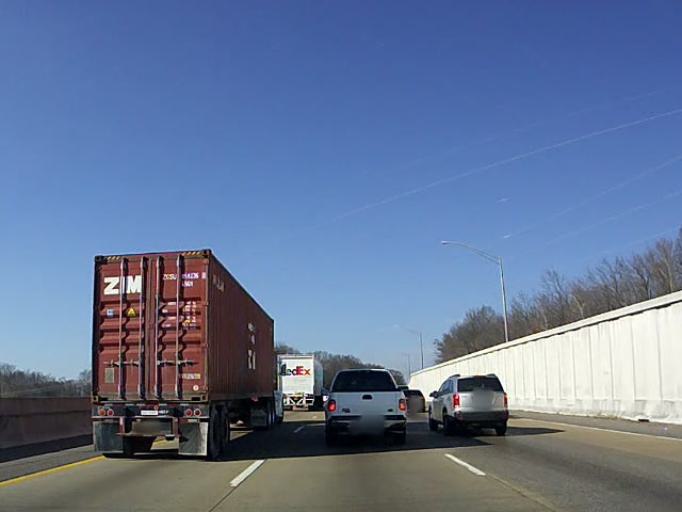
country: US
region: Tennessee
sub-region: Shelby County
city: Germantown
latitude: 35.0787
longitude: -89.8716
